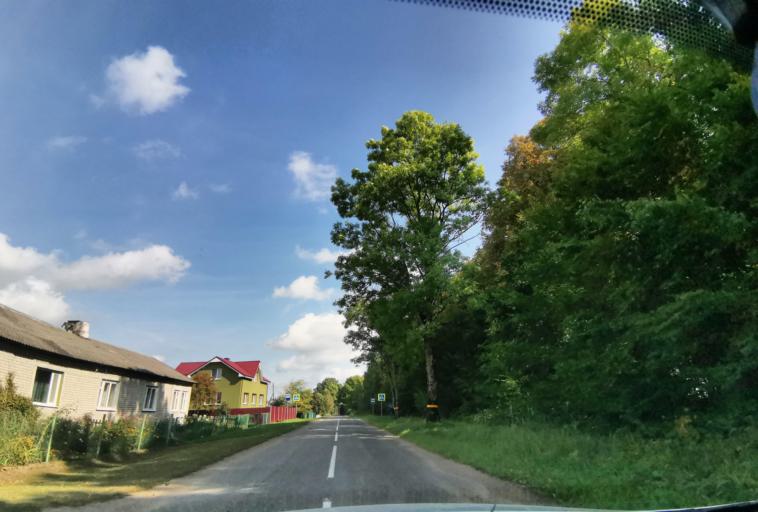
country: RU
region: Kaliningrad
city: Chernyakhovsk
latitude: 54.6574
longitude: 21.9055
